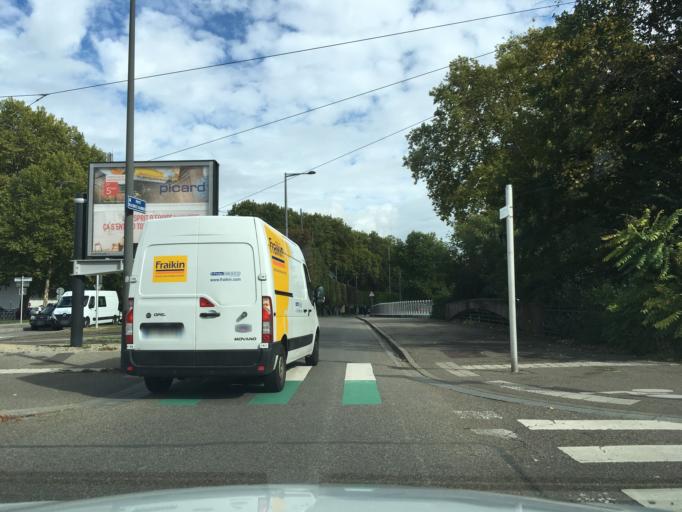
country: FR
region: Alsace
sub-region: Departement du Bas-Rhin
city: Schiltigheim
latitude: 48.6001
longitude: 7.7544
